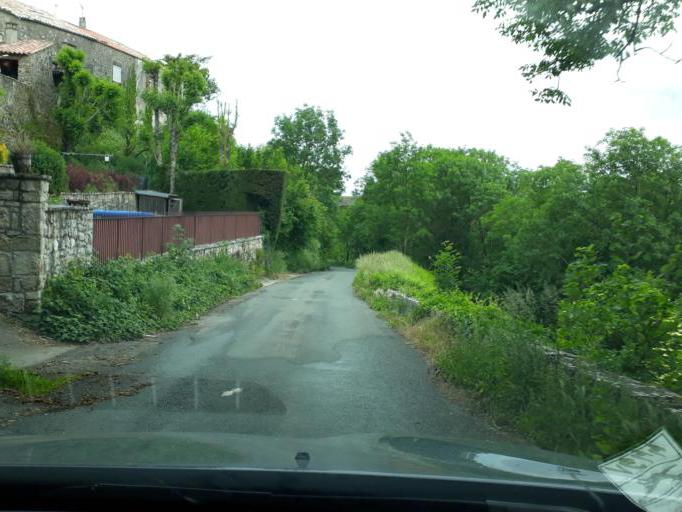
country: FR
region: Languedoc-Roussillon
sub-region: Departement de l'Herault
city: Lodeve
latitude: 43.8417
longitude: 3.2708
